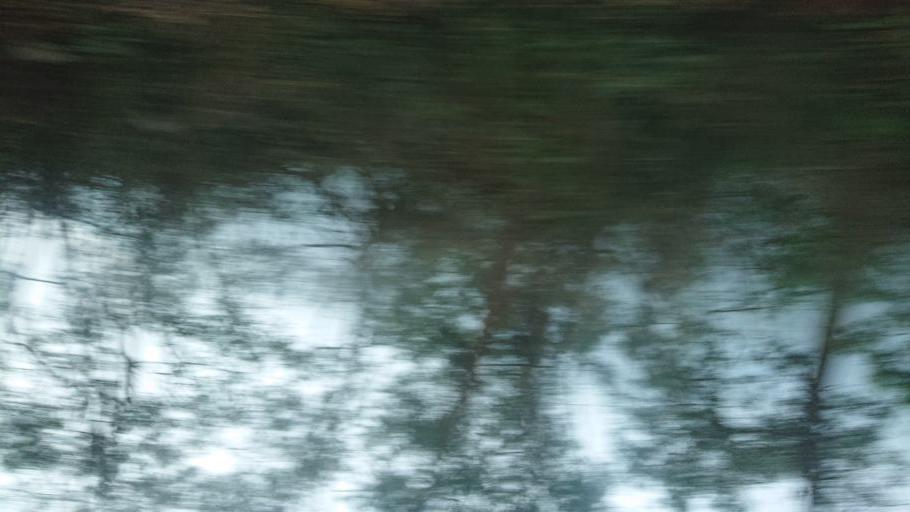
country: TW
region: Taiwan
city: Lugu
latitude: 23.5928
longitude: 120.7162
